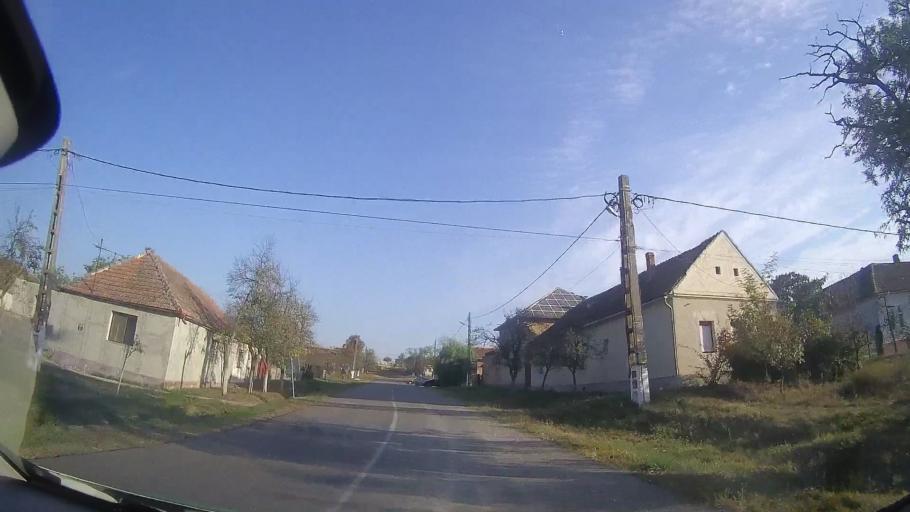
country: RO
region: Timis
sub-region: Comuna Bogda
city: Bogda
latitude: 45.9793
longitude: 21.5193
